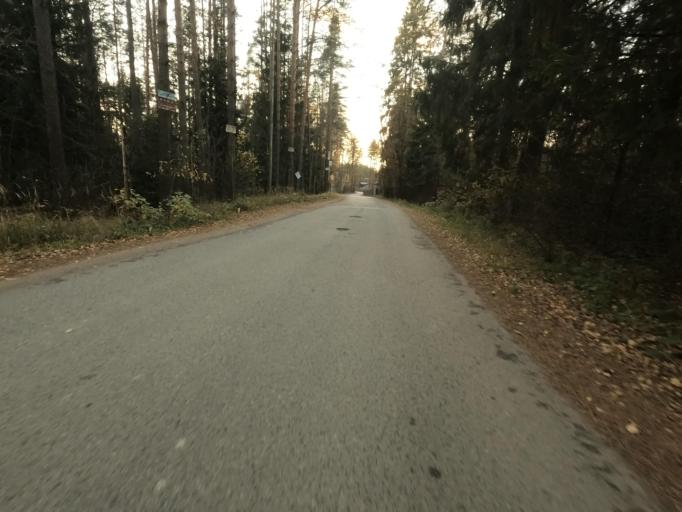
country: RU
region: Leningrad
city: Kurortnyy
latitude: 60.1939
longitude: 29.9032
